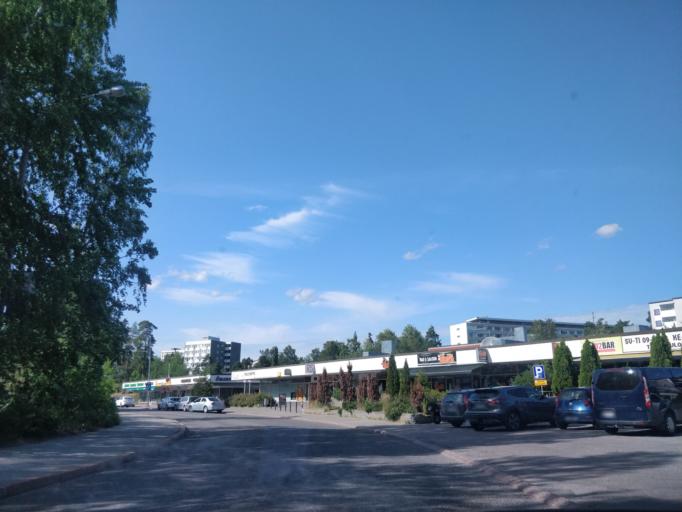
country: FI
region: Uusimaa
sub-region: Helsinki
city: Vantaa
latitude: 60.2333
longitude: 25.0115
